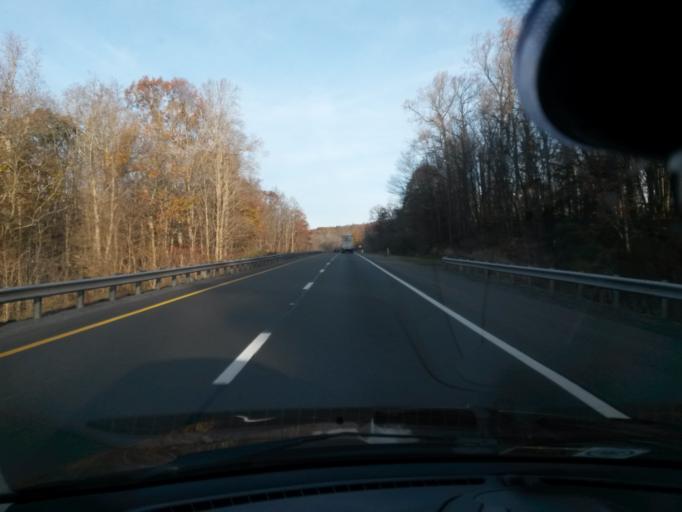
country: US
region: West Virginia
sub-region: Greenbrier County
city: Lewisburg
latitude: 37.8241
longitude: -80.4432
